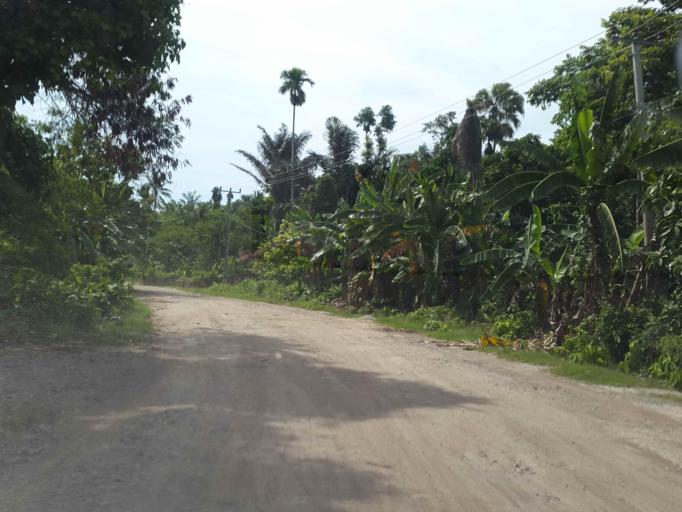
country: ID
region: Banten
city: Citeureup
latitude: -6.4969
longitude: 105.6557
